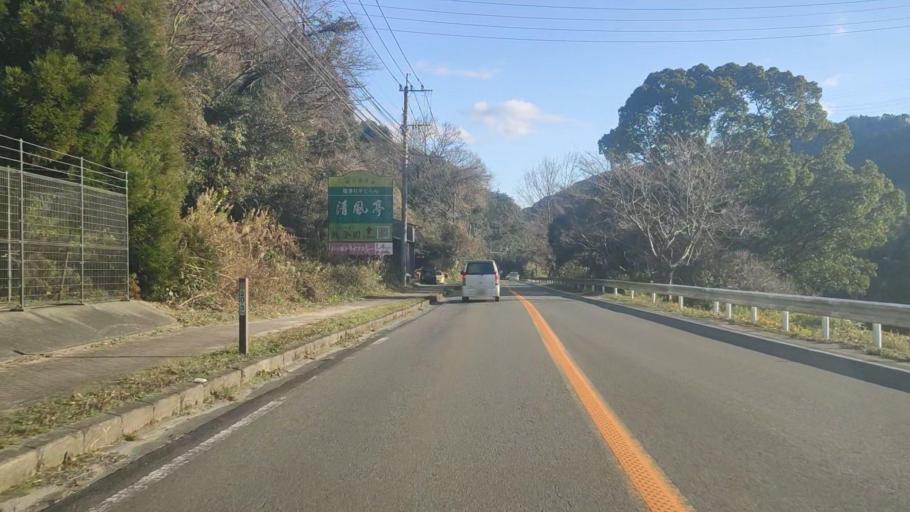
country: JP
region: Saga Prefecture
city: Saga-shi
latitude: 33.3363
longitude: 130.2611
